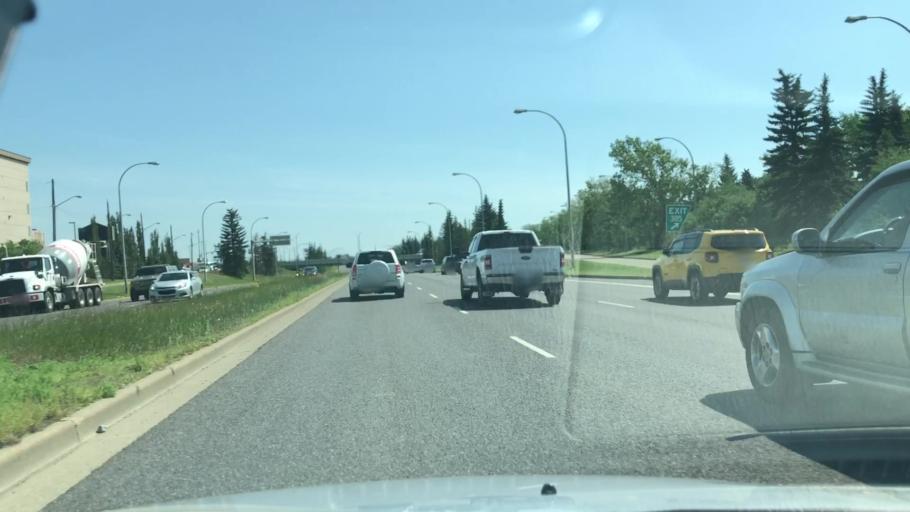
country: CA
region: Alberta
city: St. Albert
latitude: 53.5811
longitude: -113.5620
